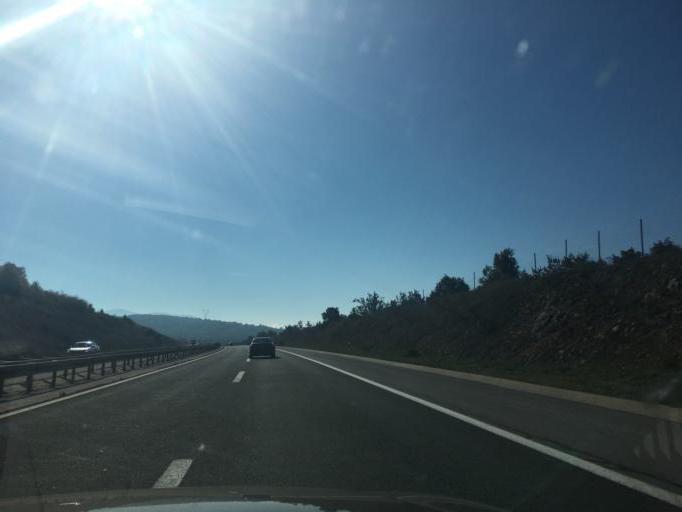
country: HR
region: Licko-Senjska
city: Gospic
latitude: 44.6567
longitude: 15.4279
